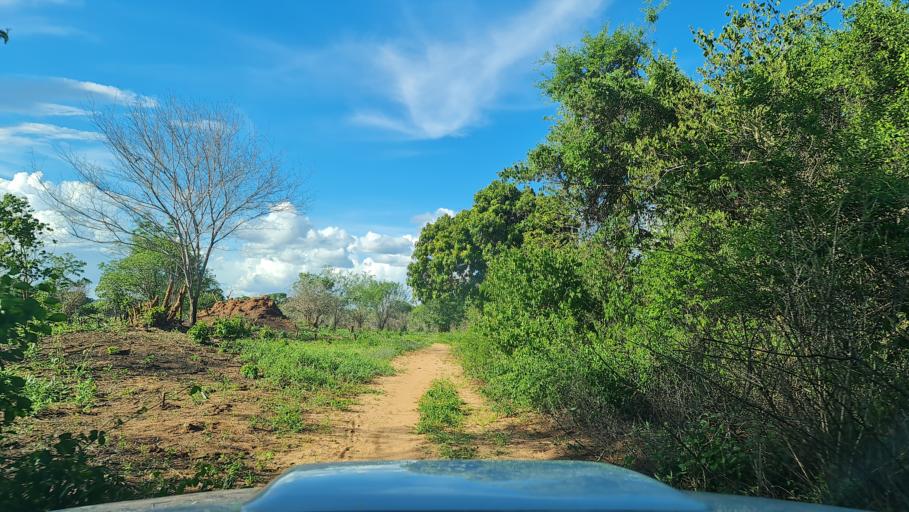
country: MZ
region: Nampula
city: Ilha de Mocambique
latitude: -15.2511
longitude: 40.1811
